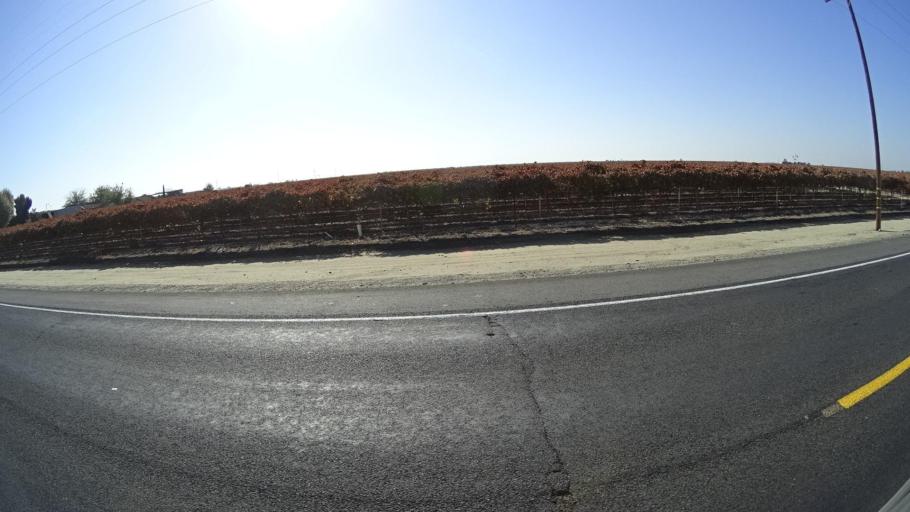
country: US
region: California
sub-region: Kern County
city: Delano
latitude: 35.7179
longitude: -119.2691
